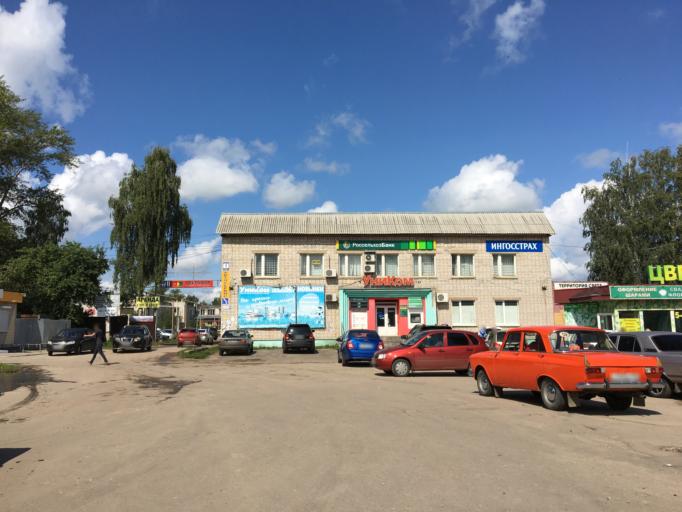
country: RU
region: Nizjnij Novgorod
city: Lyskovo
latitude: 56.0159
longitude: 45.0363
